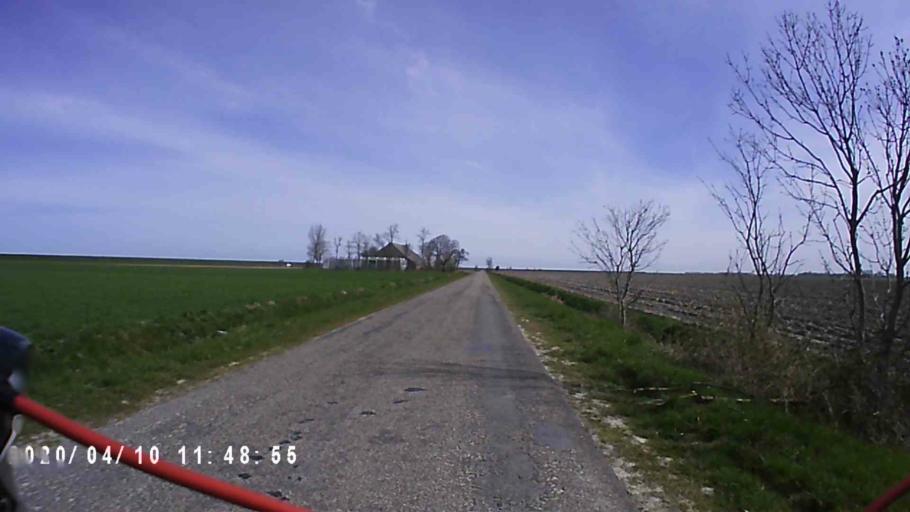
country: NL
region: Groningen
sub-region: Gemeente De Marne
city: Ulrum
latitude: 53.3875
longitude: 6.3107
